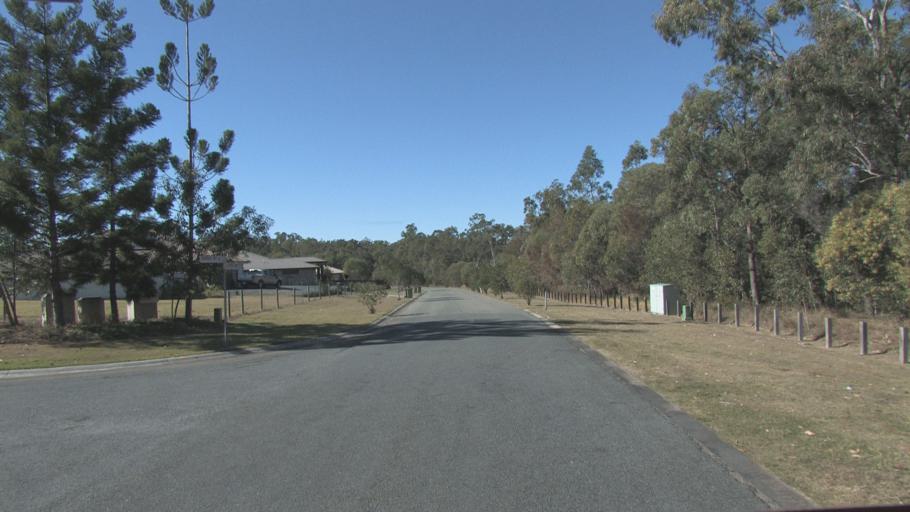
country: AU
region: Queensland
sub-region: Logan
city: North Maclean
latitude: -27.7509
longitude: 152.9660
